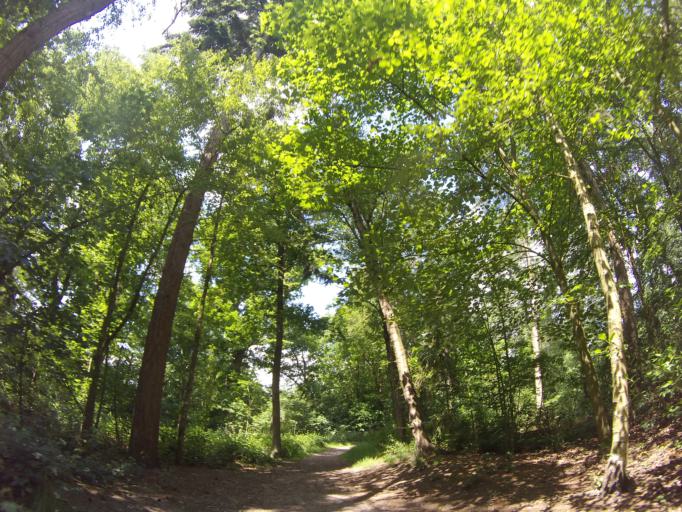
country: NL
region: Gelderland
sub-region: Gemeente Barneveld
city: Voorthuizen
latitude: 52.1915
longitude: 5.6178
